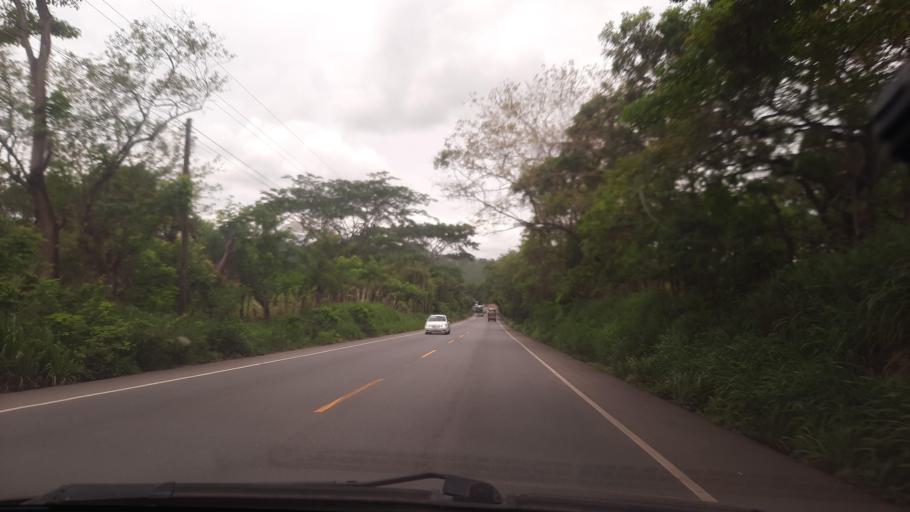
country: GT
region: Zacapa
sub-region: Municipio de Zacapa
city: Gualan
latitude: 15.1687
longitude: -89.3076
